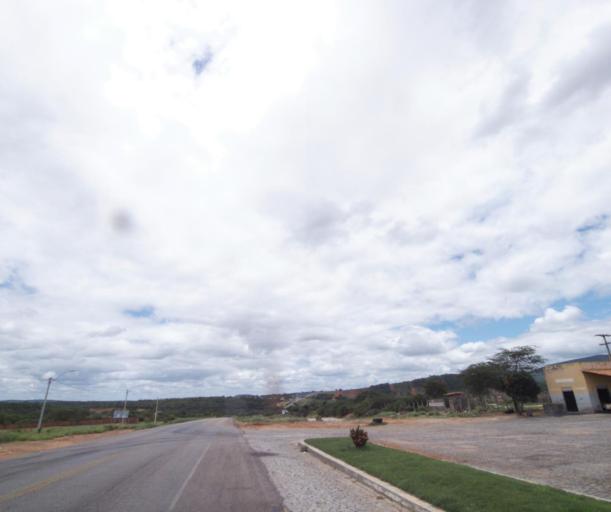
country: BR
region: Bahia
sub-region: Brumado
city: Brumado
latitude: -14.2277
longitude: -41.6761
